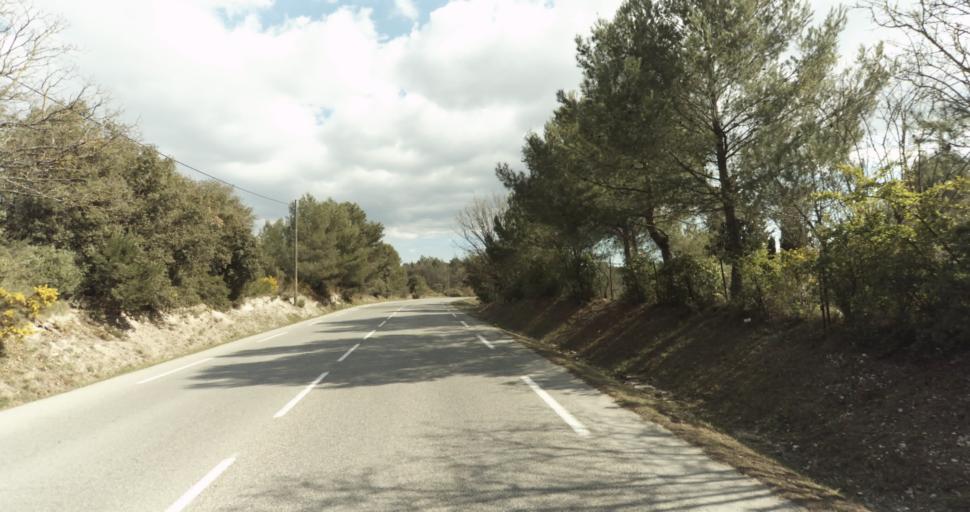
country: FR
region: Provence-Alpes-Cote d'Azur
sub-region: Departement des Bouches-du-Rhone
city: Greasque
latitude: 43.4430
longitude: 5.5269
